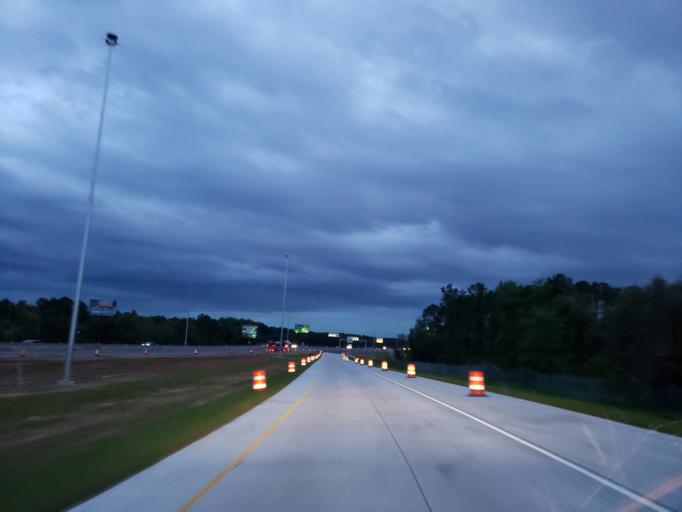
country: US
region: Georgia
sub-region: Lowndes County
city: Hahira
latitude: 30.9905
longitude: -83.3884
